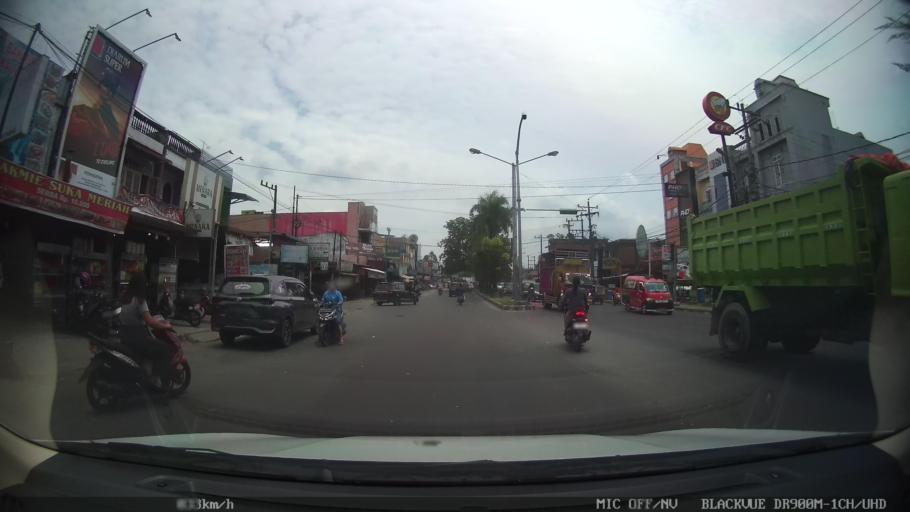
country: ID
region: North Sumatra
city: Sunggal
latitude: 3.5262
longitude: 98.6329
